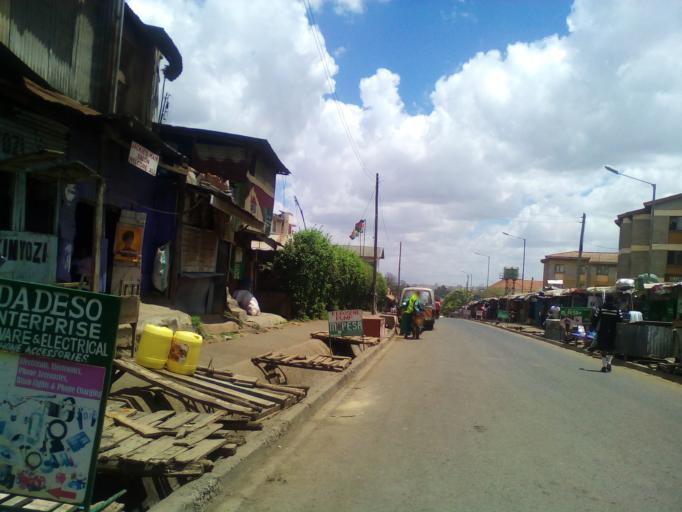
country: KE
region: Nairobi Area
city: Nairobi
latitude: -1.3151
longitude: 36.8049
